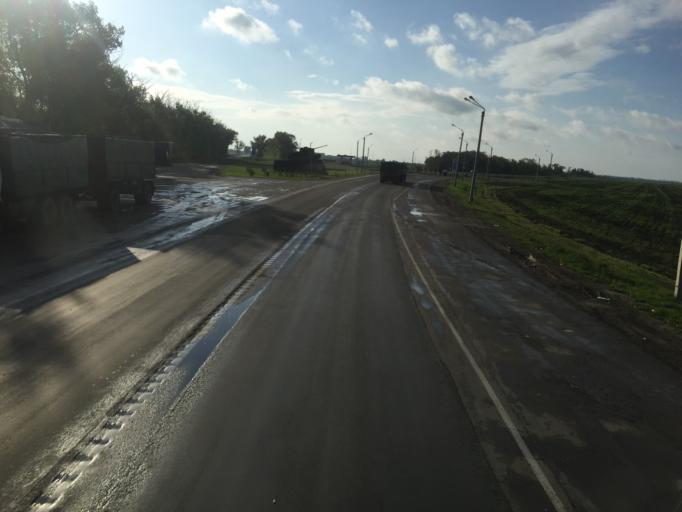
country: RU
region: Rostov
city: Yegorlykskaya
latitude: 46.5883
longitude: 40.6310
